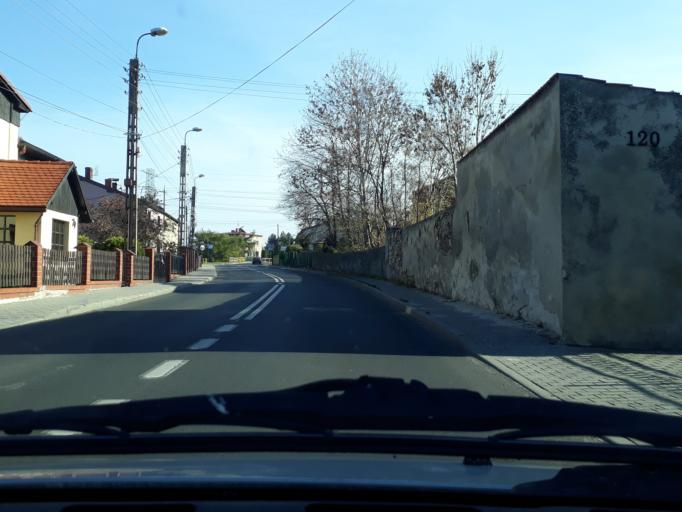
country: PL
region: Silesian Voivodeship
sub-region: Powiat tarnogorski
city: Radzionkow
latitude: 50.4205
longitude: 18.8793
